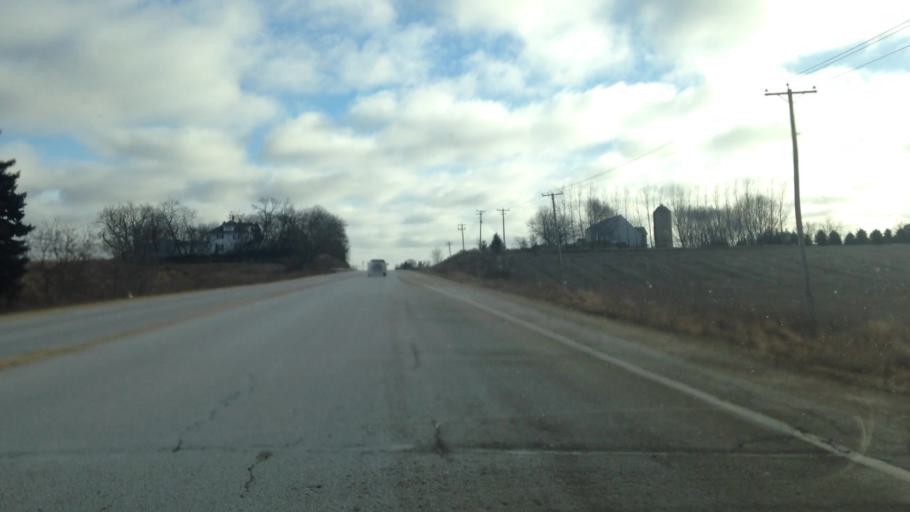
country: US
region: Wisconsin
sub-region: Dodge County
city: Mayville
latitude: 43.4427
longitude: -88.5269
